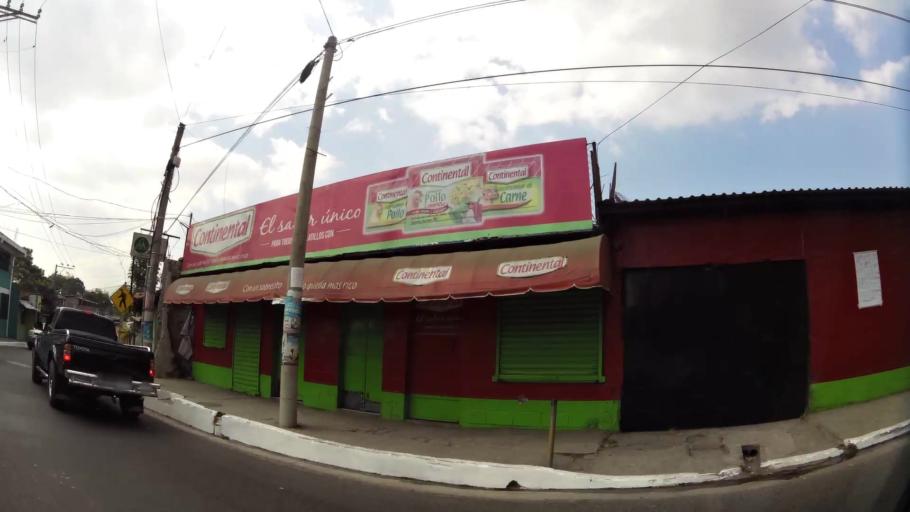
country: SV
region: San Salvador
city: Delgado
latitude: 13.7184
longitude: -89.1642
